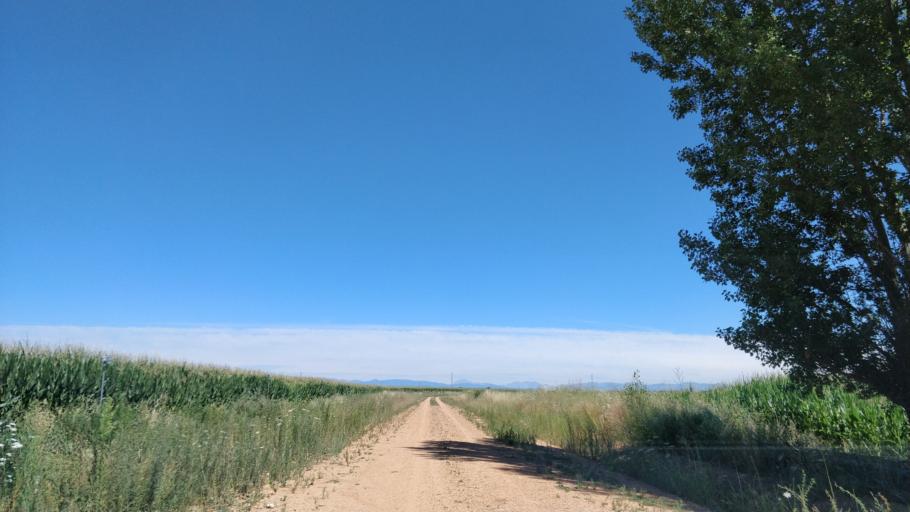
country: ES
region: Castille and Leon
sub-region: Provincia de Leon
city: Bustillo del Paramo
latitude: 42.4527
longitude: -5.8161
